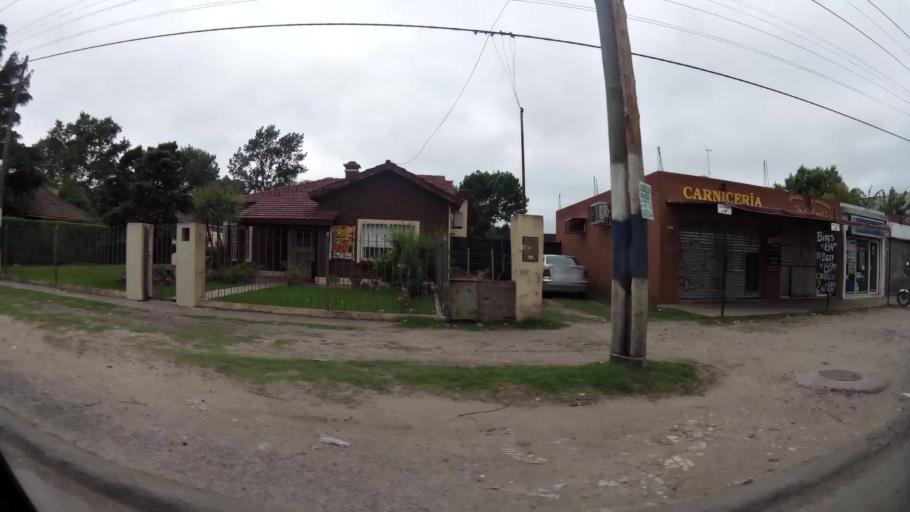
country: AR
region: Buenos Aires
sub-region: Partido de La Plata
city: La Plata
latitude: -34.9602
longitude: -58.0095
